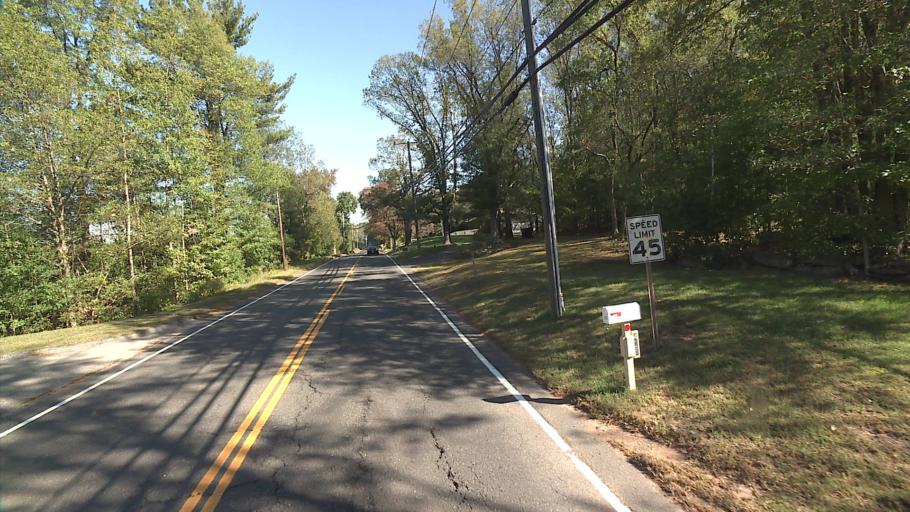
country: US
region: Connecticut
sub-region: Tolland County
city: Ellington
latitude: 41.9329
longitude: -72.4548
